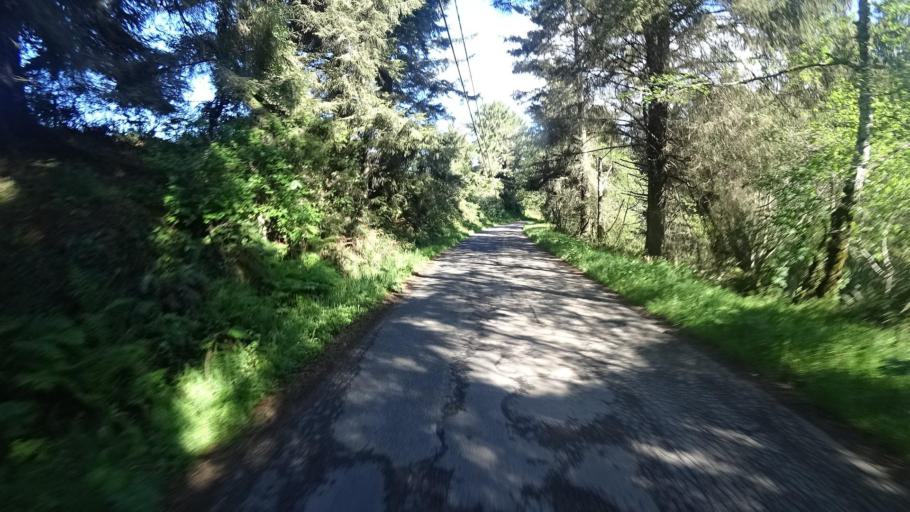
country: US
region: California
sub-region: Humboldt County
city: Westhaven-Moonstone
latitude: 41.0063
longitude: -124.1066
